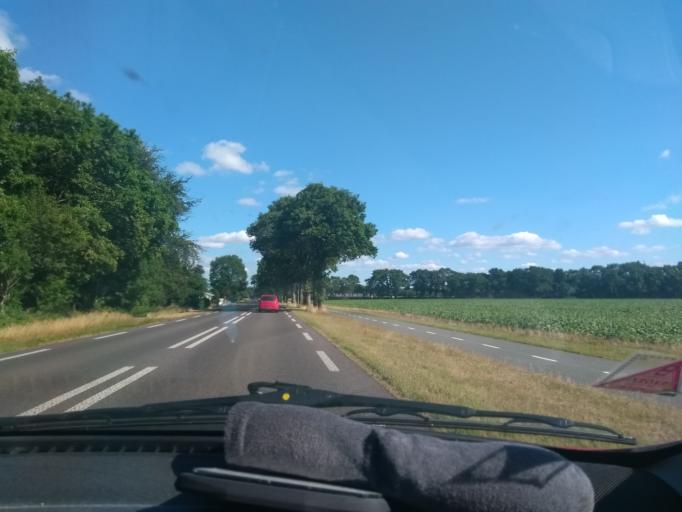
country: NL
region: Drenthe
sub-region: Gemeente Tynaarlo
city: Vries
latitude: 53.0886
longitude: 6.5588
